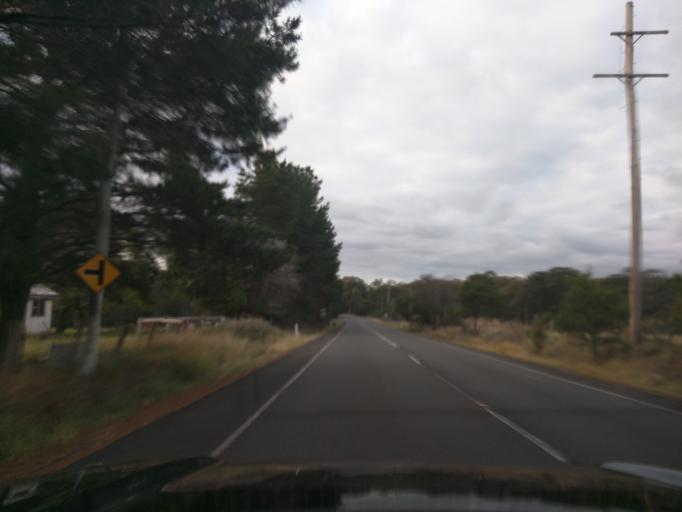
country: AU
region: New South Wales
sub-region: Wollondilly
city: Douglas Park
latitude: -34.2550
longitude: 150.7231
